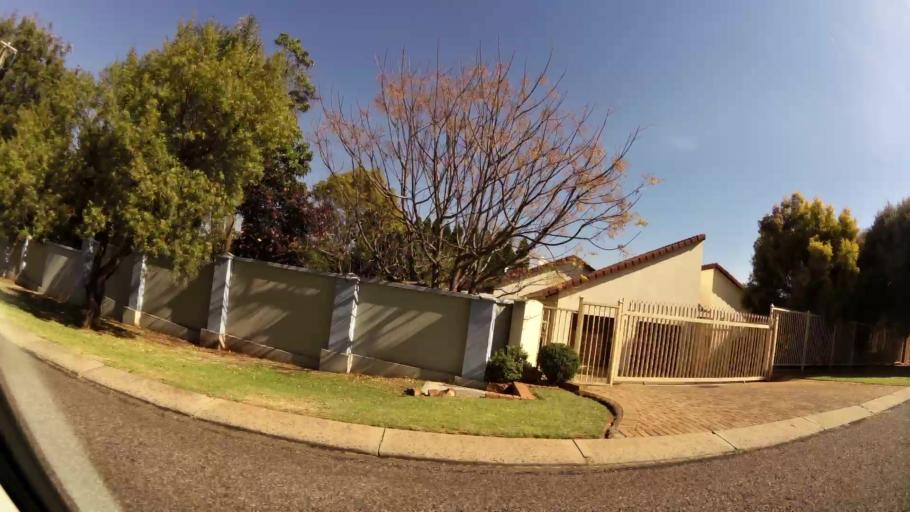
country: ZA
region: Gauteng
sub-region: City of Tshwane Metropolitan Municipality
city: Pretoria
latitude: -25.7957
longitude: 28.2298
